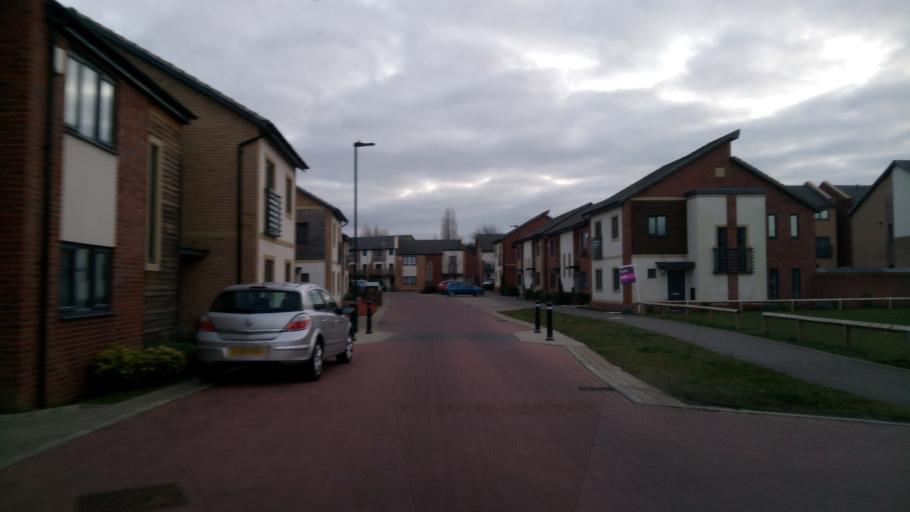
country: GB
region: England
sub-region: Peterborough
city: Peterborough
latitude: 52.5645
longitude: -0.2376
